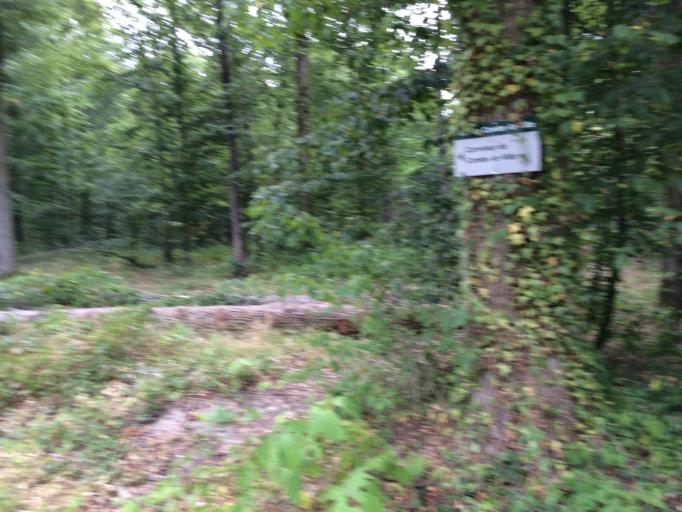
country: FR
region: Ile-de-France
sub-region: Departement de l'Essonne
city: Quincy-sous-Senart
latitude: 48.6609
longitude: 2.5407
